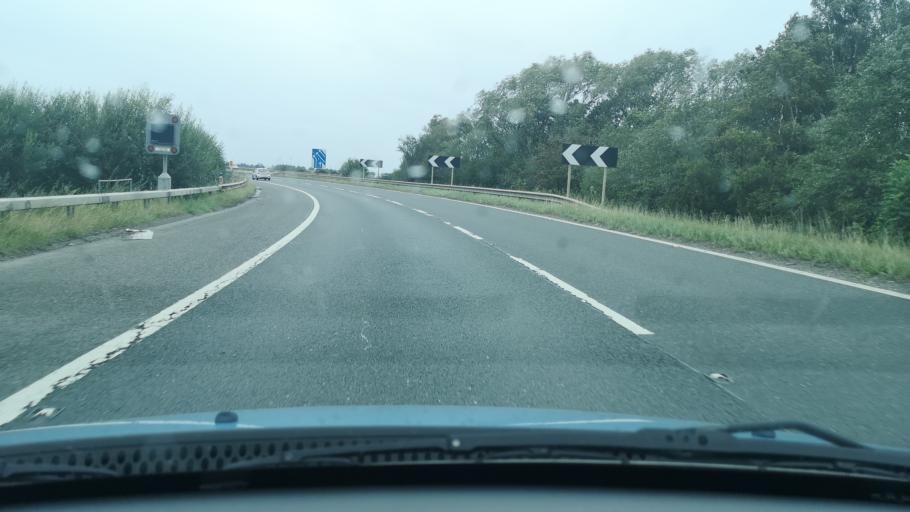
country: GB
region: England
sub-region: North Lincolnshire
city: Gunness
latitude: 53.5565
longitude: -0.7164
